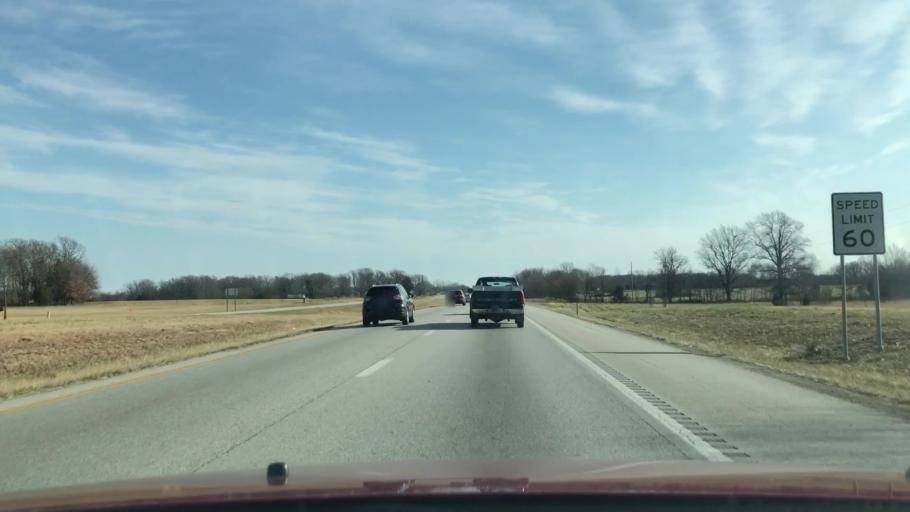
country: US
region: Missouri
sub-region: Webster County
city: Rogersville
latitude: 37.1186
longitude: -93.1171
